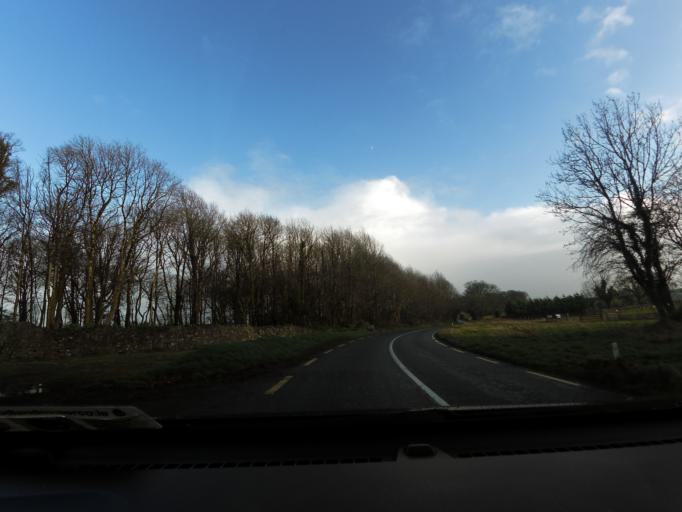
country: IE
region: Connaught
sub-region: County Galway
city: Tuam
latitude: 53.4922
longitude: -8.9606
